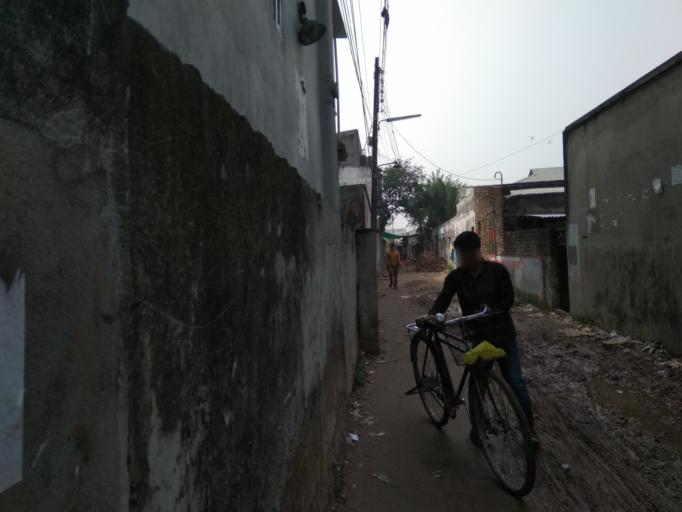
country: BD
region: Dhaka
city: Tungi
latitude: 23.8596
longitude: 90.3870
